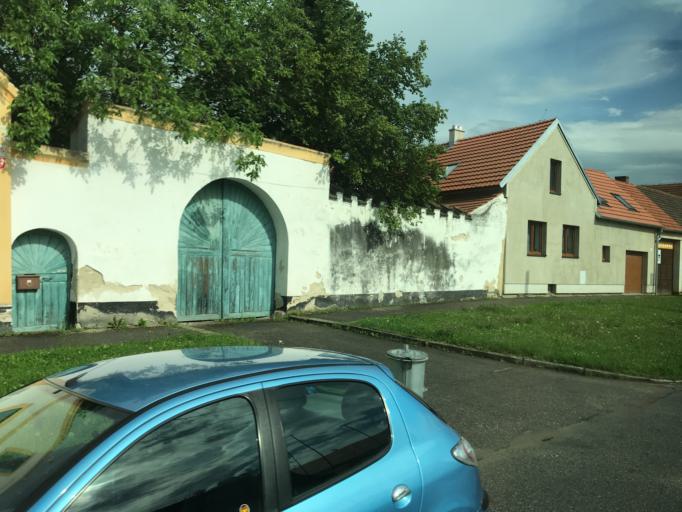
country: CZ
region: Jihocesky
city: Litvinovice
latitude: 48.9472
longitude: 14.4651
